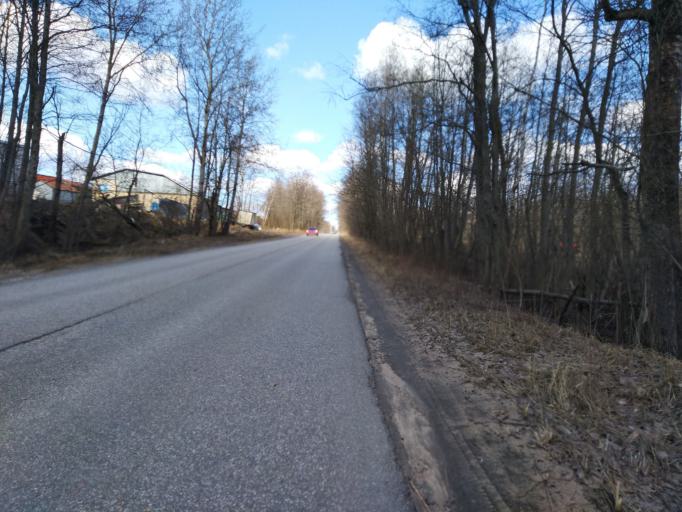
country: RU
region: Leningrad
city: Novoye Devyatkino
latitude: 60.1017
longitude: 30.4790
